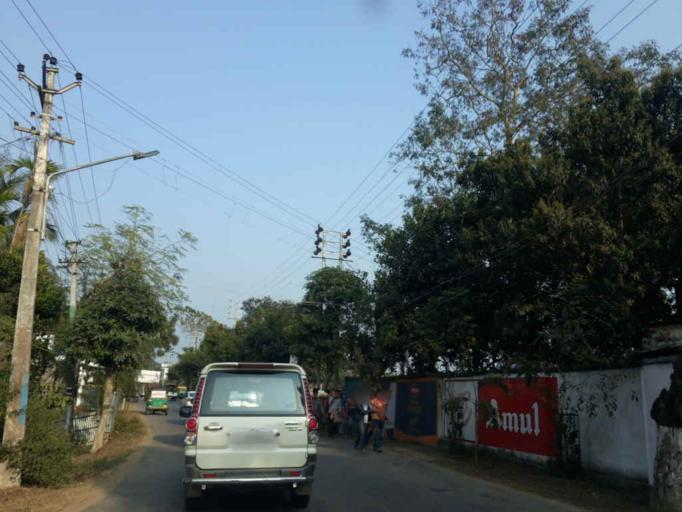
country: IN
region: Tripura
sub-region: West Tripura
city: Agartala
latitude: 23.8830
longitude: 91.2617
